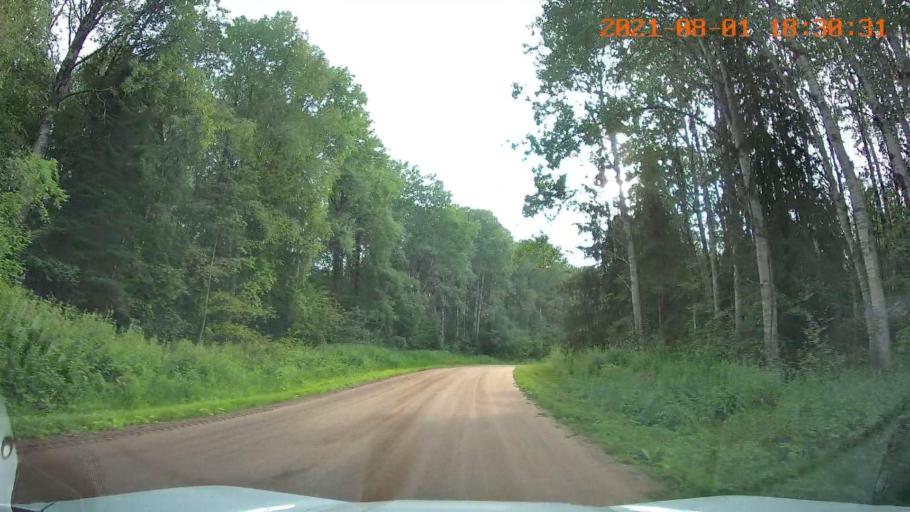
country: RU
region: Leningrad
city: Voznesen'ye
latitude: 60.8877
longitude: 35.3551
